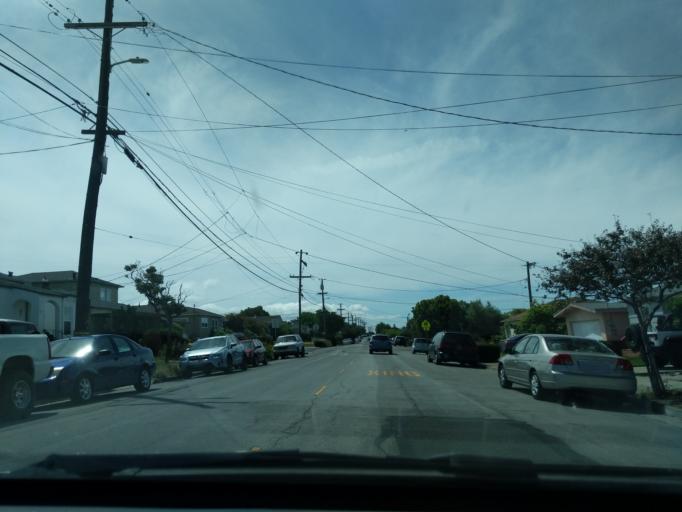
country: US
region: California
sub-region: Contra Costa County
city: El Cerrito
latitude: 37.9196
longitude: -122.3091
